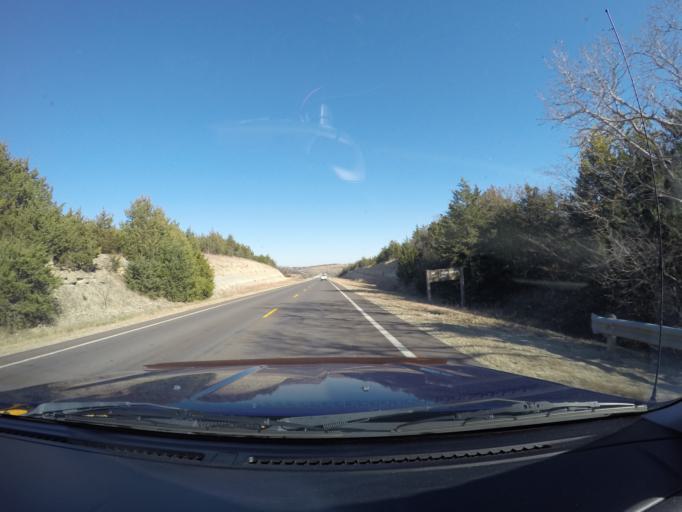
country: US
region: Kansas
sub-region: Marshall County
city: Blue Rapids
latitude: 39.4615
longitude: -96.7597
